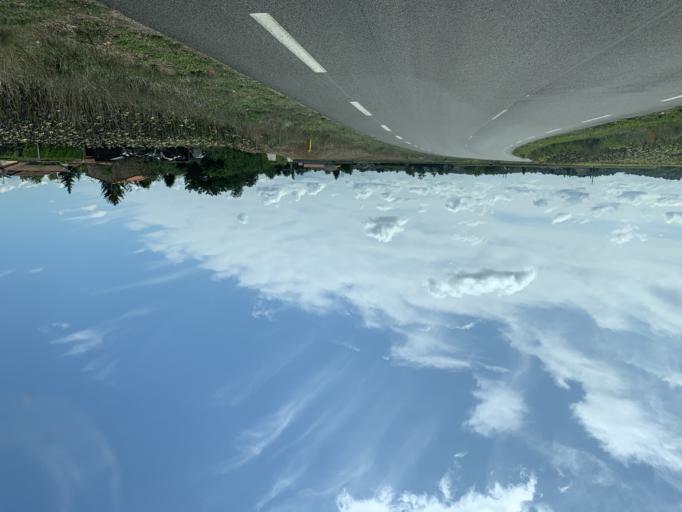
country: FR
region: Rhone-Alpes
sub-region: Departement de l'Ain
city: Nievroz
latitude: 45.8325
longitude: 5.0664
